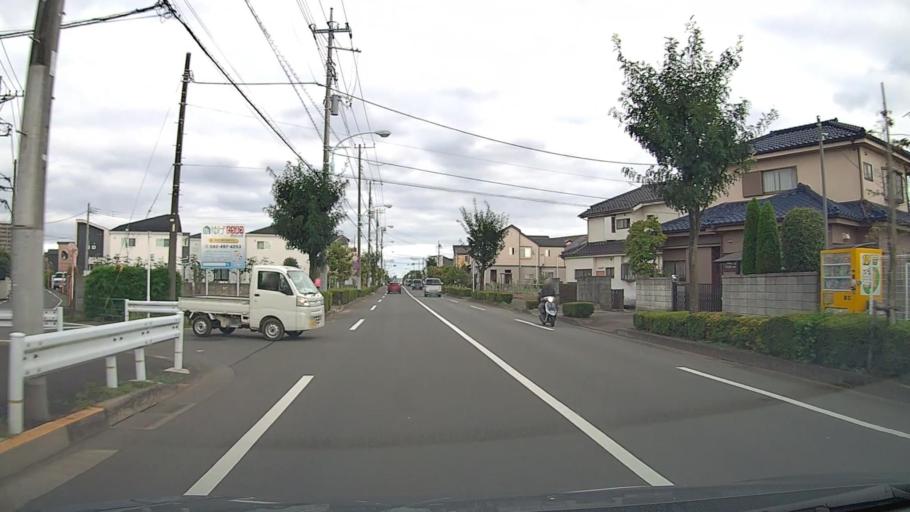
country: JP
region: Tokyo
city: Tanashicho
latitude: 35.7447
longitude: 139.5183
